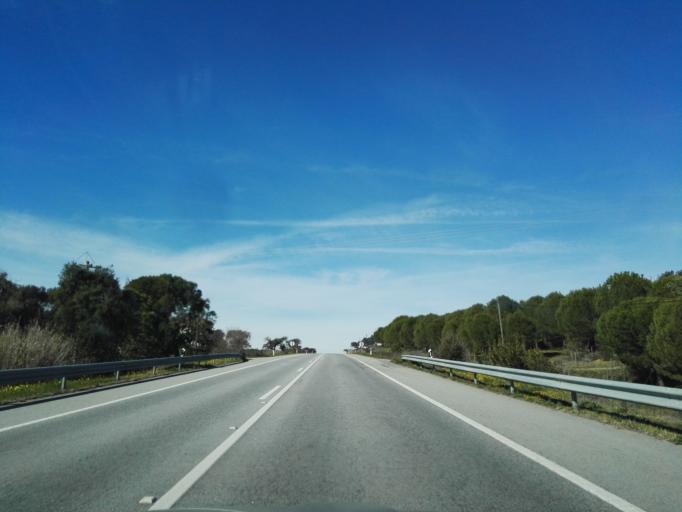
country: PT
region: Portalegre
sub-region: Arronches
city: Arronches
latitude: 39.1475
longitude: -7.3066
